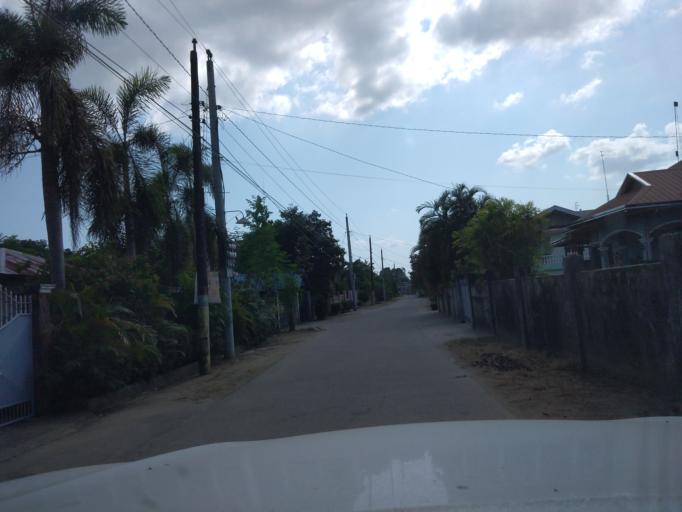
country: PH
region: Central Luzon
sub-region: Province of Pampanga
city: Candaba
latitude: 15.0877
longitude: 120.8137
